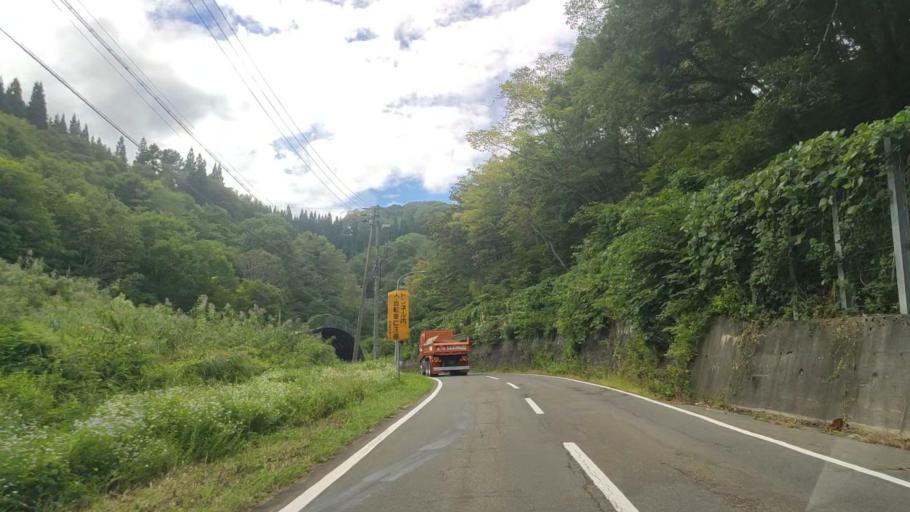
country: JP
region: Nagano
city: Iiyama
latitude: 36.8796
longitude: 138.3194
